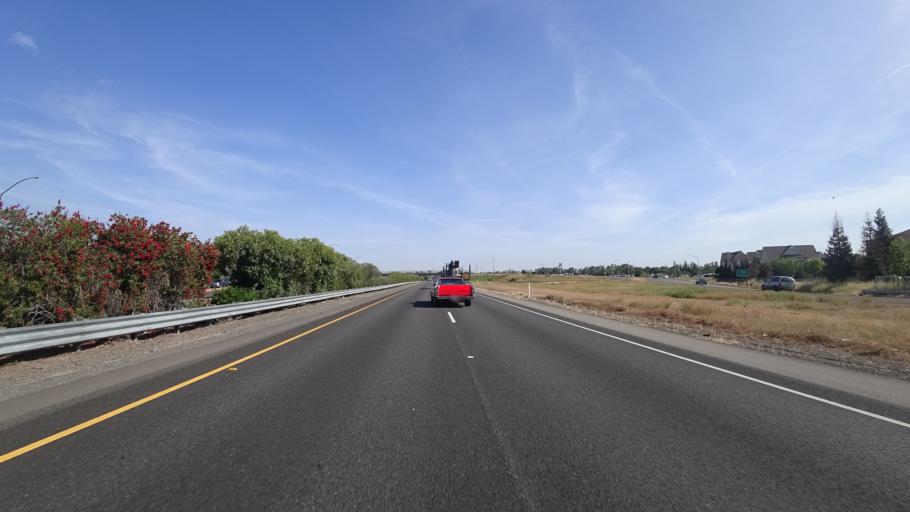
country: US
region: California
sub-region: Butte County
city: Chico
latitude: 39.7173
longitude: -121.8027
